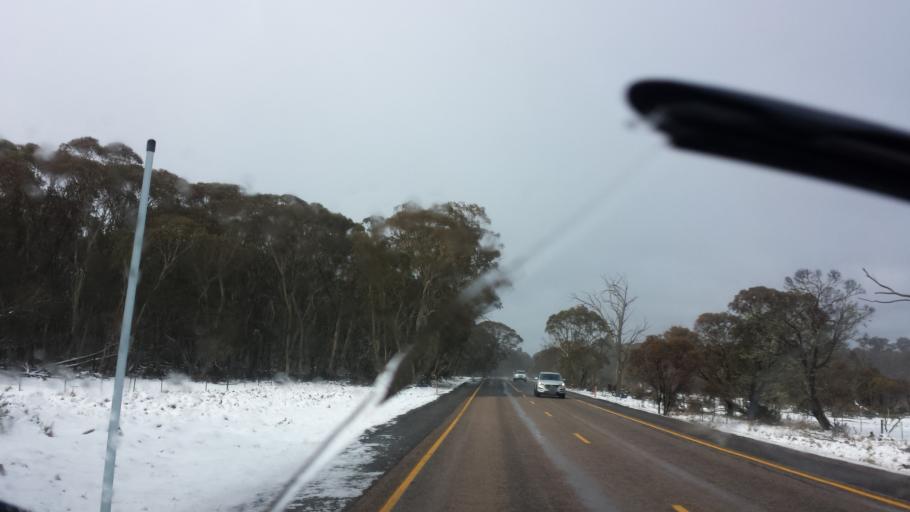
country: AU
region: Victoria
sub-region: Alpine
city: Mount Beauty
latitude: -37.0332
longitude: 147.3005
